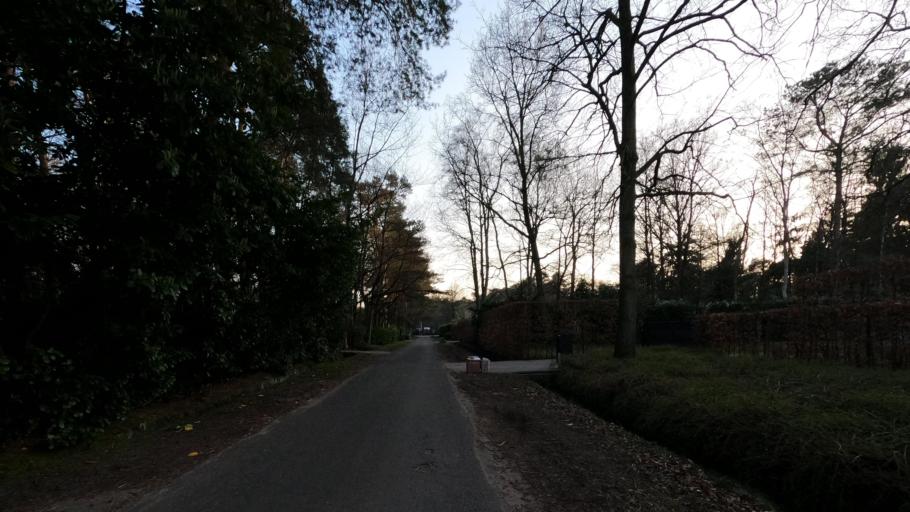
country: BE
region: Flanders
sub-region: Provincie Antwerpen
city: Schilde
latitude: 51.2815
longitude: 4.6218
